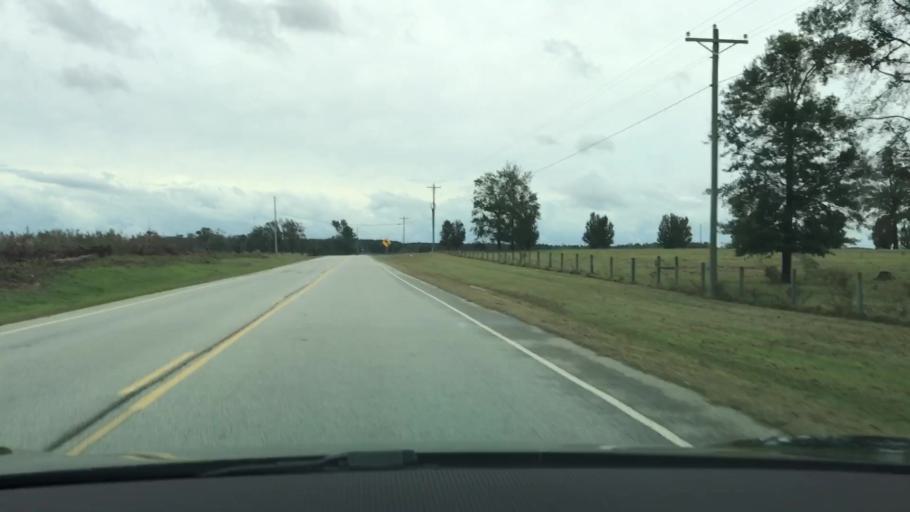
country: US
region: Georgia
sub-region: Jefferson County
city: Wrens
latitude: 33.1210
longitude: -82.4454
